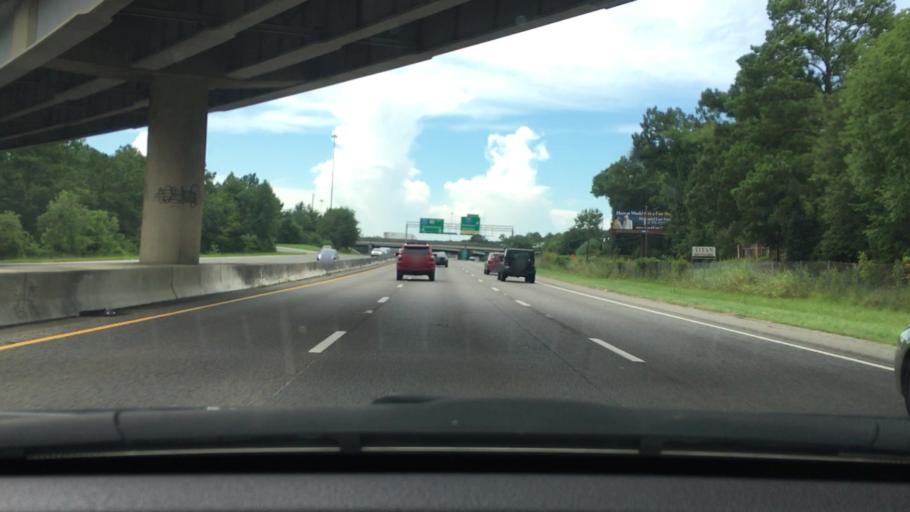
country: US
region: South Carolina
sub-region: Lexington County
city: Saint Andrews
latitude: 34.0255
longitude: -81.0990
